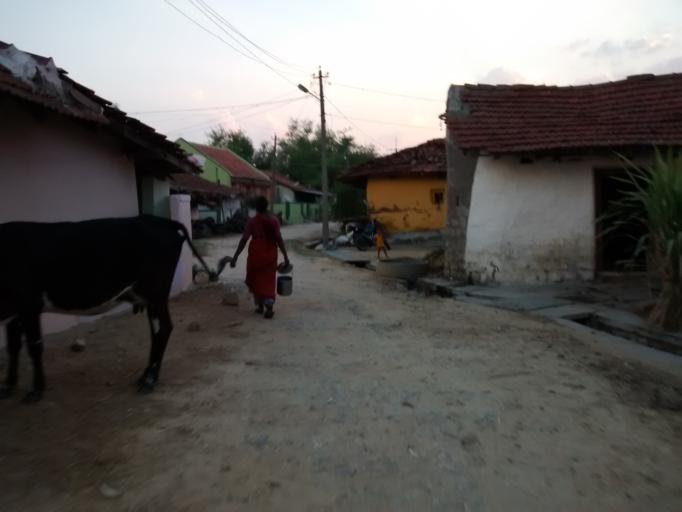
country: IN
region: Karnataka
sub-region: Hassan
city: Hassan
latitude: 12.9430
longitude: 76.1586
